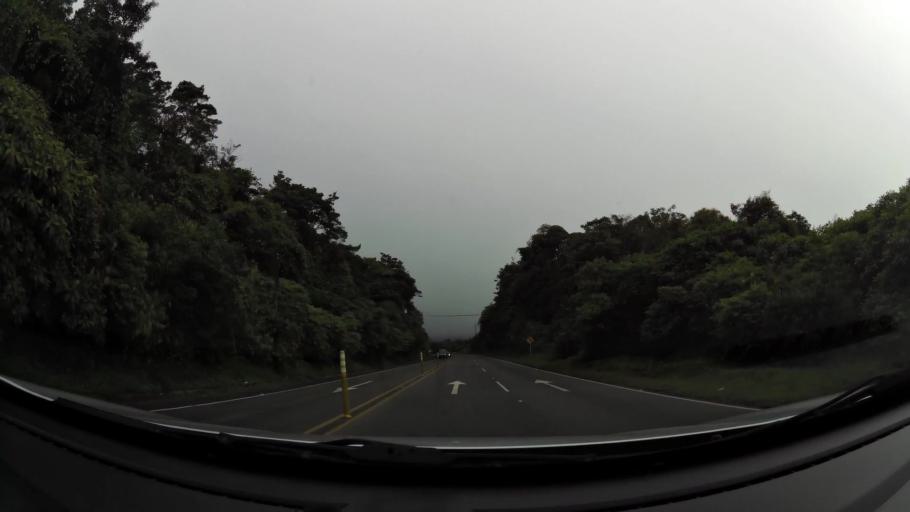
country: CR
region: Heredia
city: Angeles
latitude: 10.0391
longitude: -84.0038
